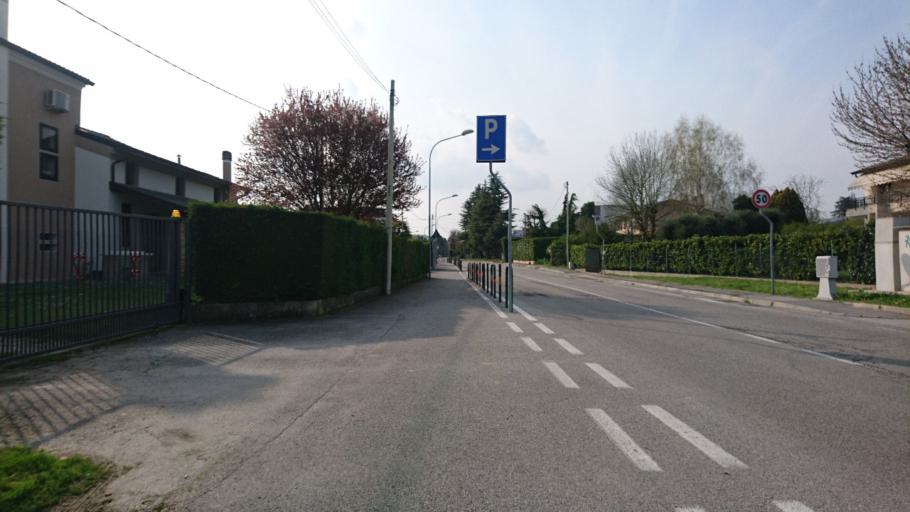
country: IT
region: Veneto
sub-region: Provincia di Padova
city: San Vito
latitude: 45.4109
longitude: 11.9662
